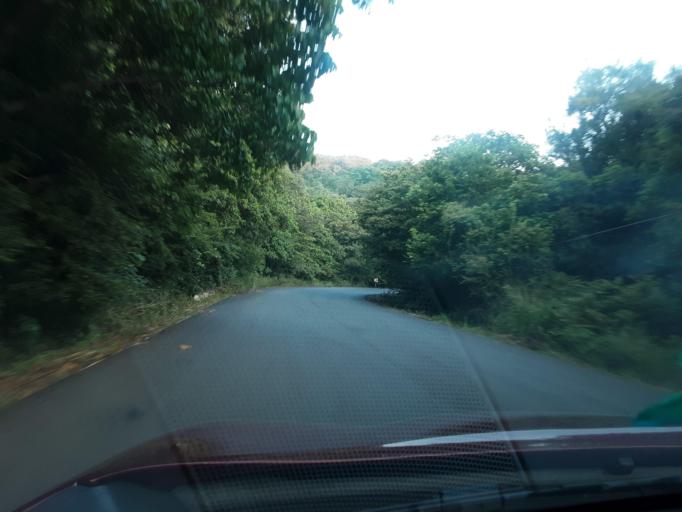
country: LK
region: Central
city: Dambulla
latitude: 7.8142
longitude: 80.7654
